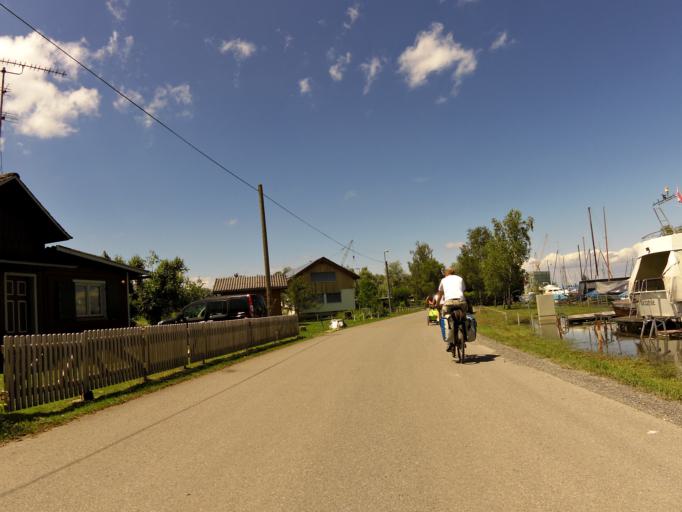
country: AT
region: Vorarlberg
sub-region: Politischer Bezirk Bregenz
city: Fussach
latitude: 47.4874
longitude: 9.6639
